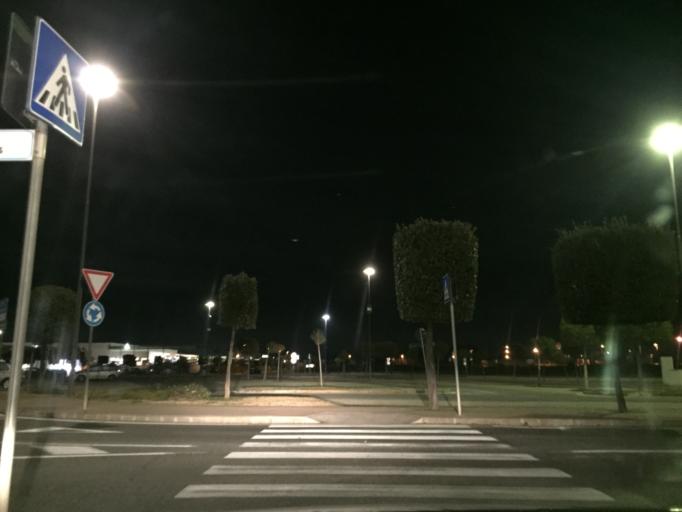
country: IT
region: Latium
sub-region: Citta metropolitana di Roma Capitale
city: Npp 23 (Parco Leonardo)
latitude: 41.8081
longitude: 12.3020
